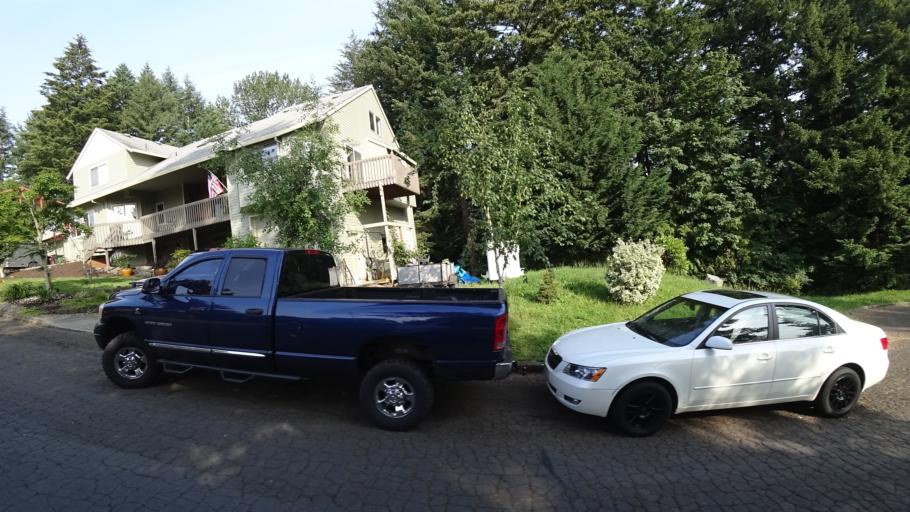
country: US
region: Oregon
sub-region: Clackamas County
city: Happy Valley
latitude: 45.4568
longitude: -122.5339
